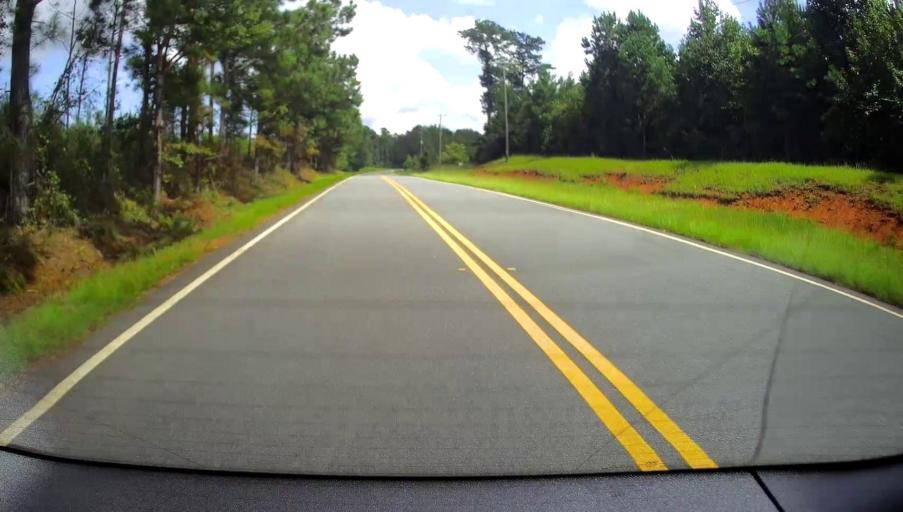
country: US
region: Georgia
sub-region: Bibb County
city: West Point
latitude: 32.8680
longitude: -83.9047
